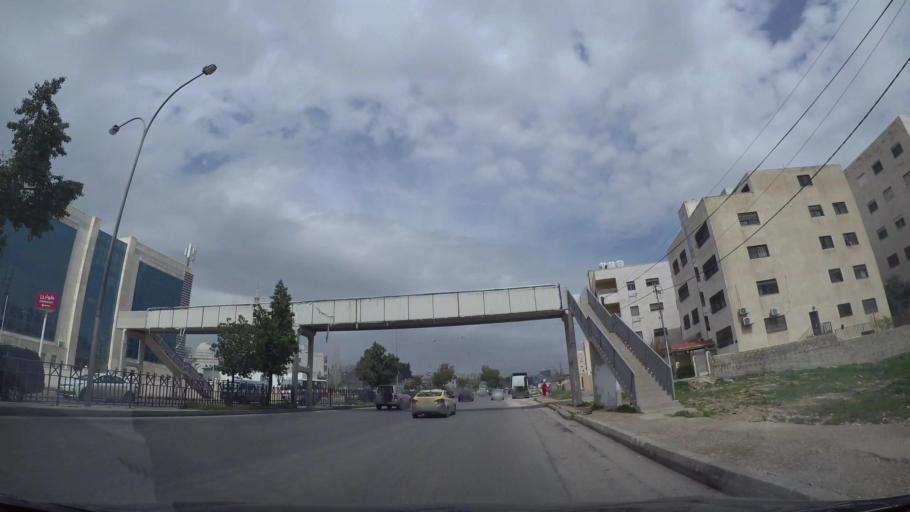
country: JO
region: Amman
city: Amman
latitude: 31.9886
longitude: 35.9179
